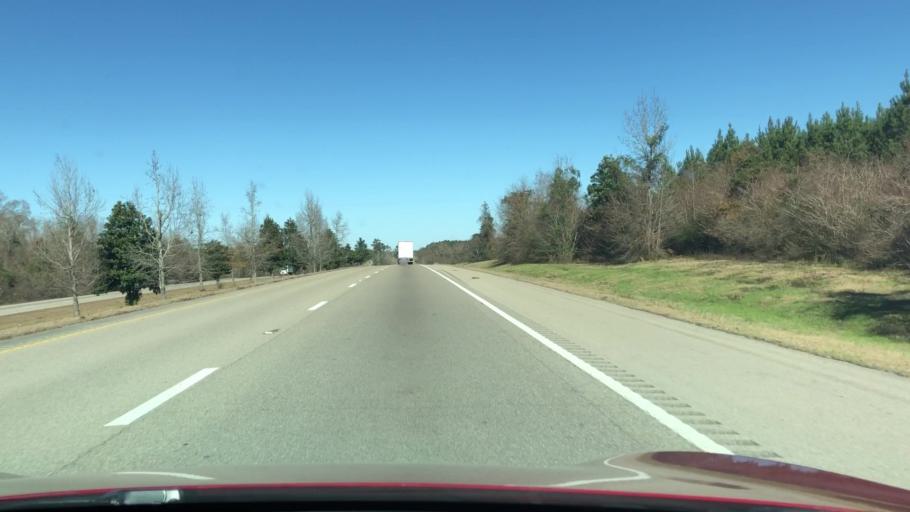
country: US
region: Mississippi
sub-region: Pearl River County
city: Poplarville
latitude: 30.7711
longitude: -89.5210
